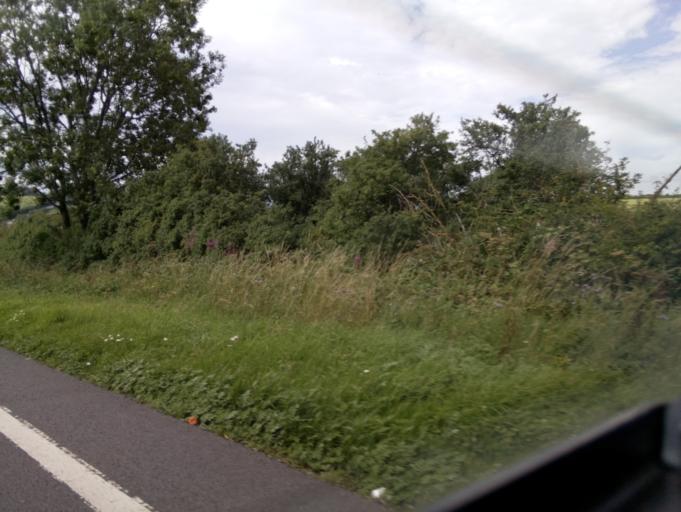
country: GB
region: England
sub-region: Somerset
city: Yeovil
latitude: 50.8297
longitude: -2.5713
